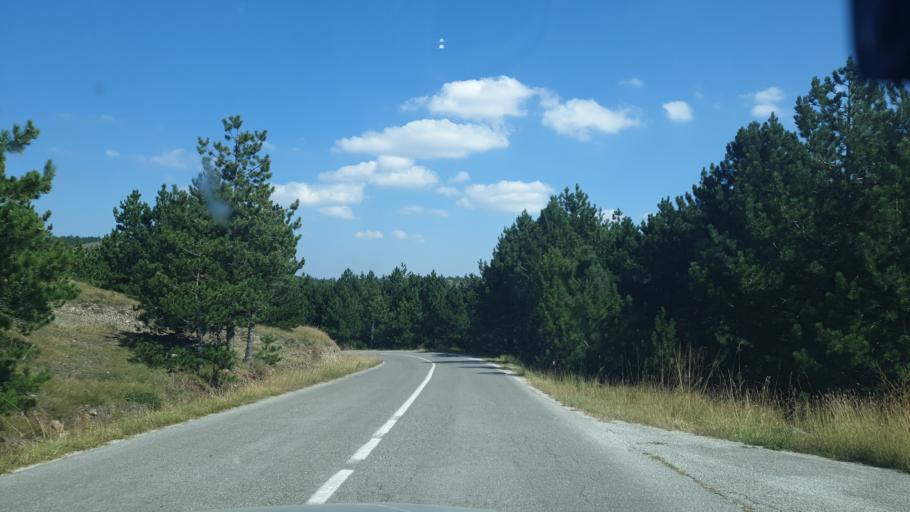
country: RS
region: Central Serbia
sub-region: Zlatiborski Okrug
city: Kosjeric
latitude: 44.0870
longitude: 20.0052
